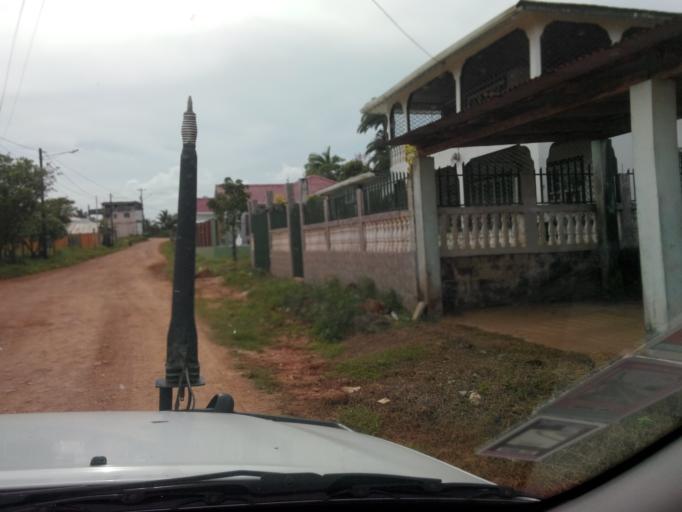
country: NI
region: Atlantico Sur
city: Bluefields
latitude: 12.0309
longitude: -83.7668
